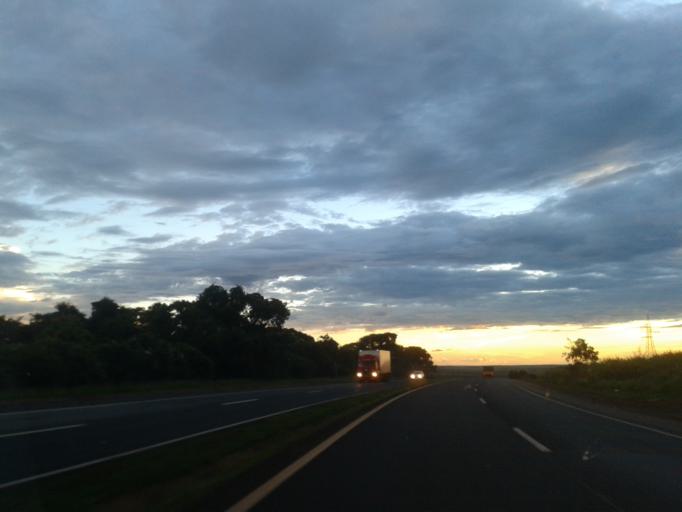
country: BR
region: Minas Gerais
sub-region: Monte Alegre De Minas
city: Monte Alegre de Minas
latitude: -18.7744
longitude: -49.0741
